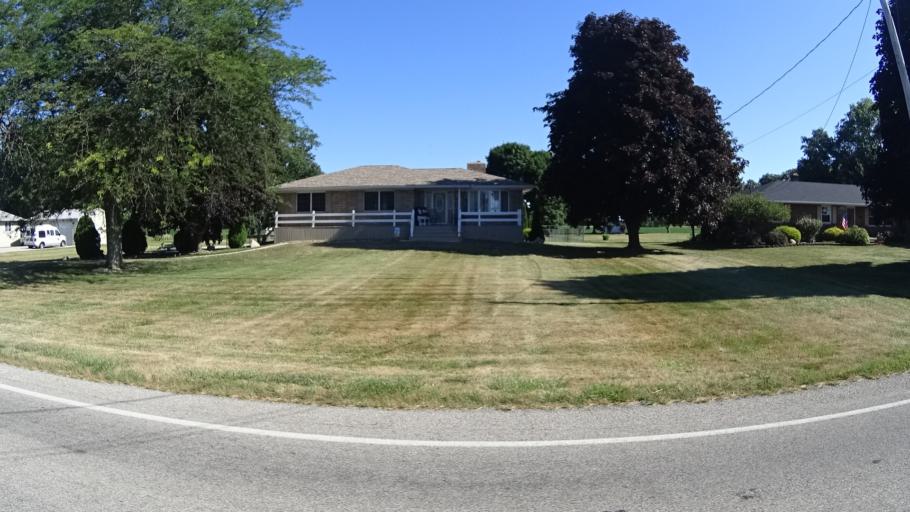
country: US
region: Ohio
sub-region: Erie County
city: Sandusky
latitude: 41.3969
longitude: -82.7246
